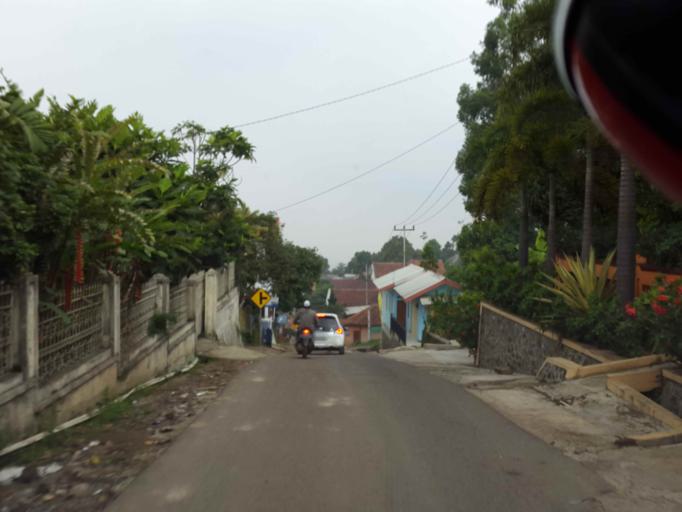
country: ID
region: West Java
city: Lembang
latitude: -6.8370
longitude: 107.5854
